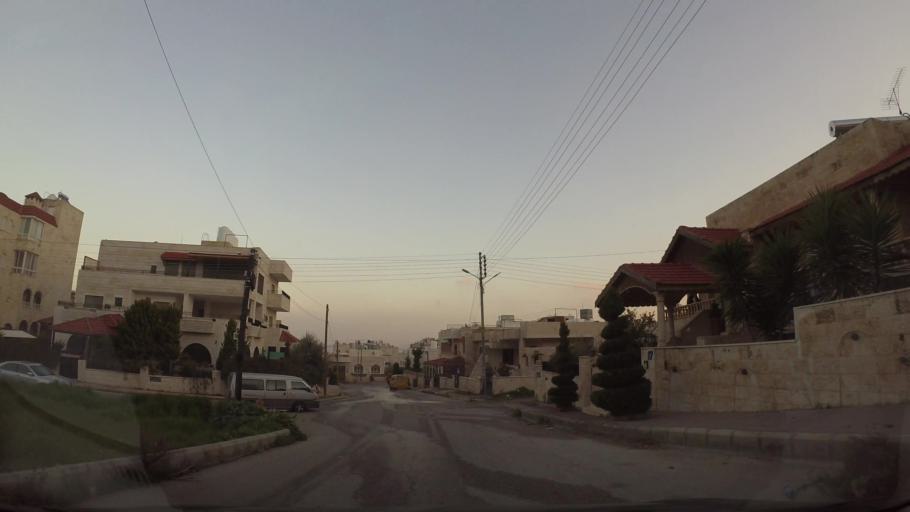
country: JO
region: Amman
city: Amman
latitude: 31.9965
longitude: 35.9494
